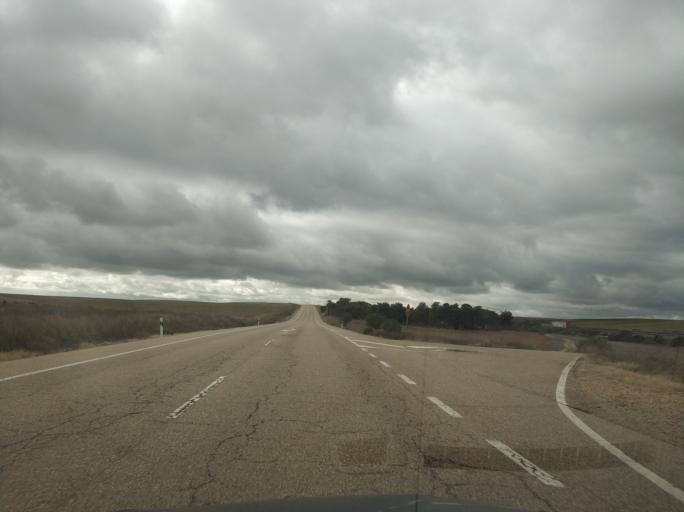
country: ES
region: Castille and Leon
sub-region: Provincia de Valladolid
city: Torrecilla de la Orden
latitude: 41.2665
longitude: -5.2632
